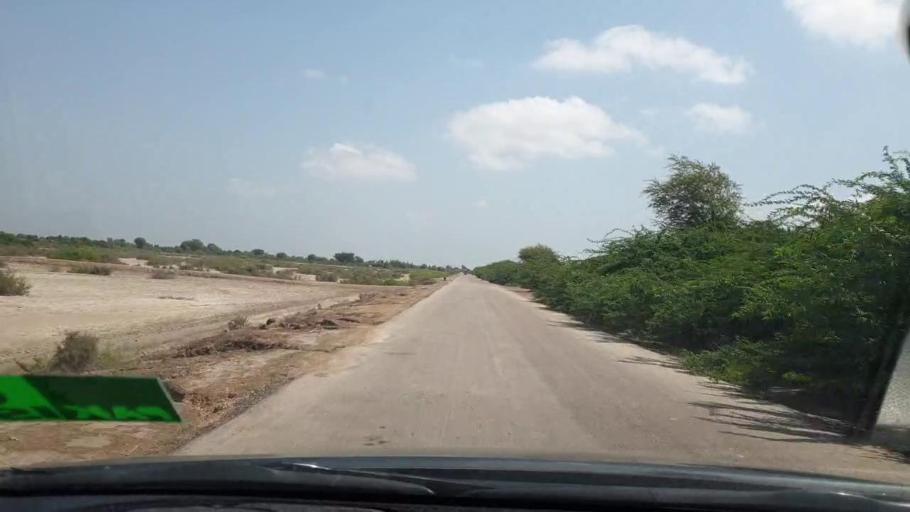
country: PK
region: Sindh
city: Digri
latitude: 25.0011
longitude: 69.1388
